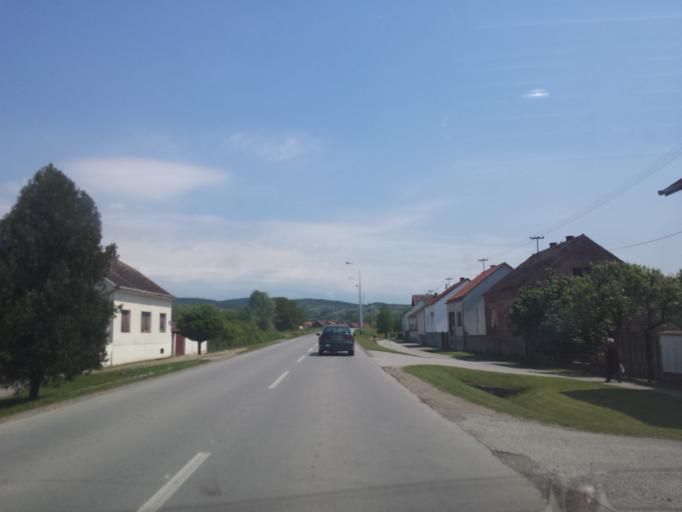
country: HR
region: Brodsko-Posavska
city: Luzani
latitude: 45.1683
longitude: 17.7059
